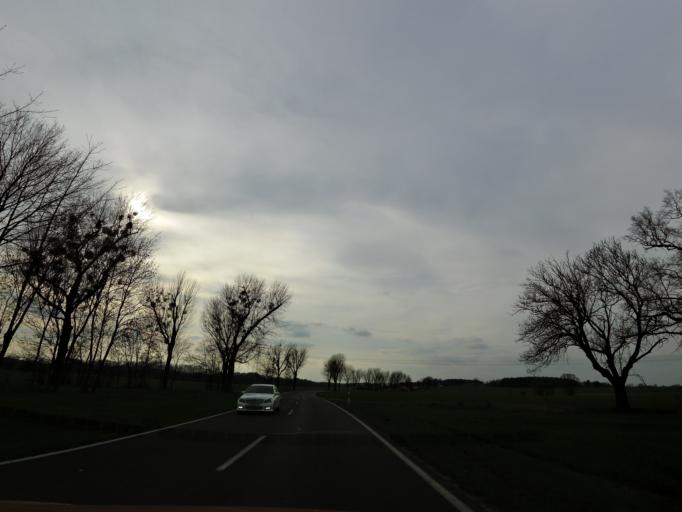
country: DE
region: Brandenburg
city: Mittenwalde
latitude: 52.2512
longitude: 13.5607
